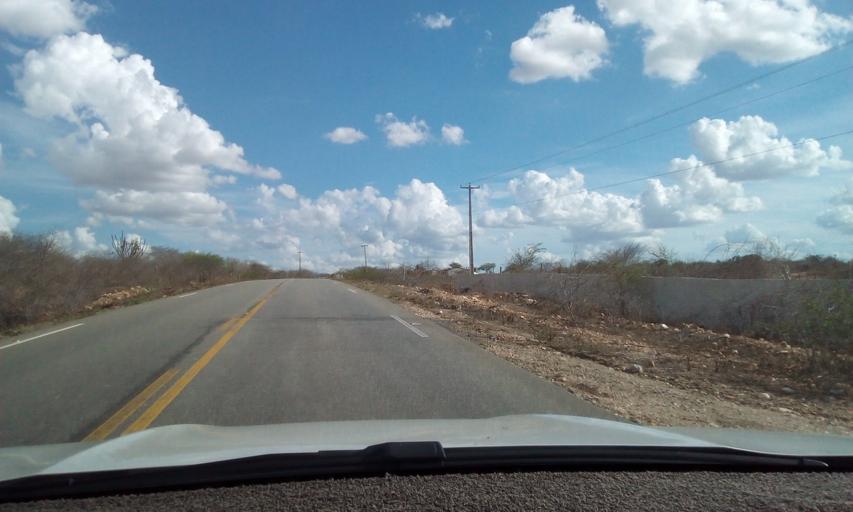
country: BR
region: Paraiba
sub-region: Soledade
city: Soledade
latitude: -6.8008
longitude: -36.4039
